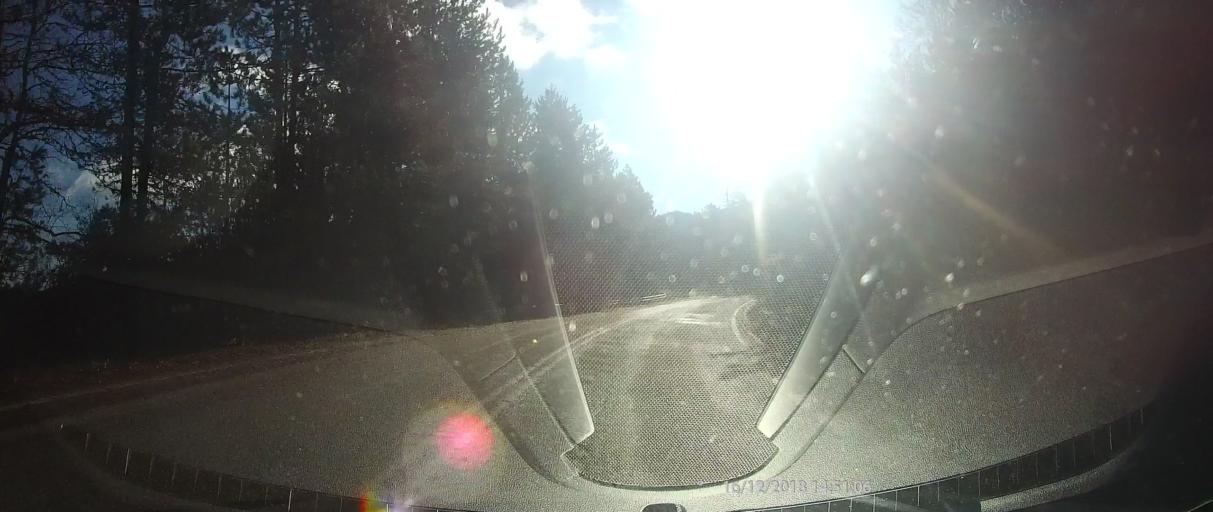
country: GR
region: West Macedonia
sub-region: Nomos Kastorias
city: Nestorio
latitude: 40.2072
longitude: 21.0744
